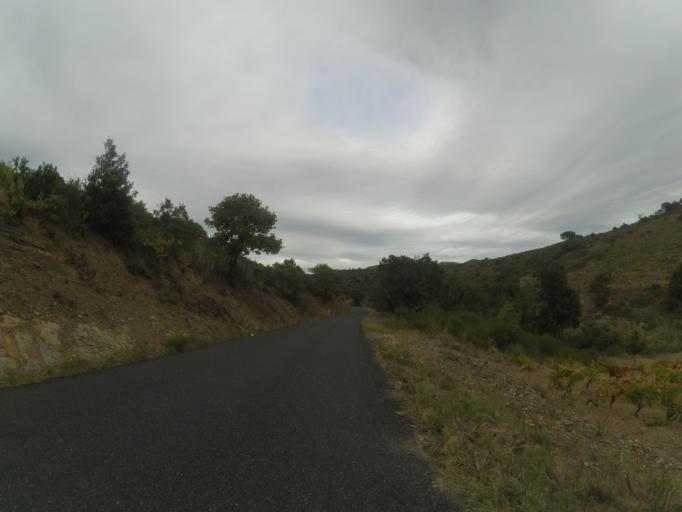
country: FR
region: Languedoc-Roussillon
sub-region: Departement des Pyrenees-Orientales
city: Estagel
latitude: 42.7457
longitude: 2.7248
